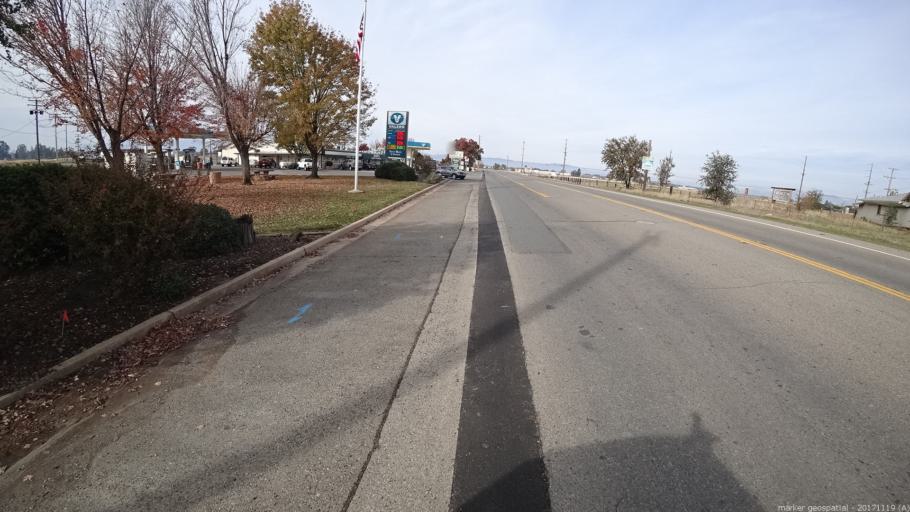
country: US
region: California
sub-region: Shasta County
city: Anderson
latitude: 40.4896
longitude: -122.2940
